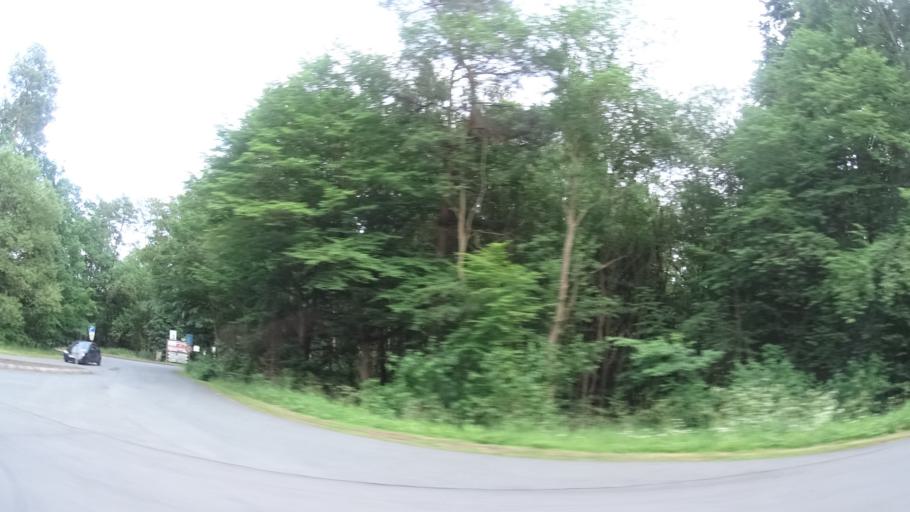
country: DE
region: Hesse
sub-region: Regierungsbezirk Kassel
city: Bad Arolsen
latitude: 51.3714
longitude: 9.0533
